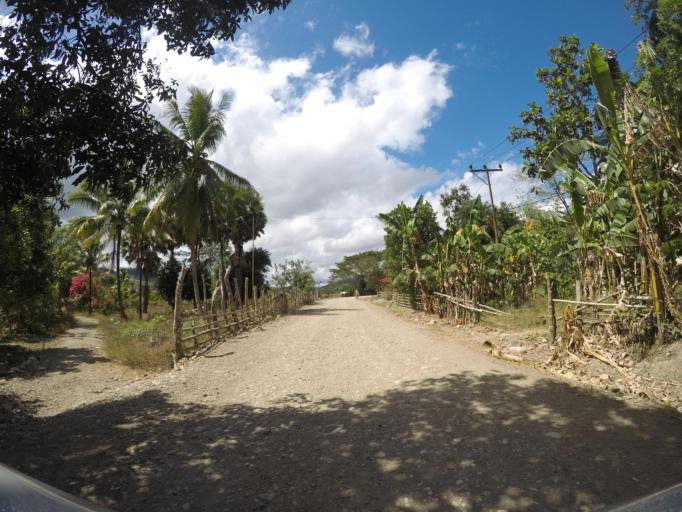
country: TL
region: Lautem
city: Lospalos
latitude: -8.4856
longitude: 126.8191
